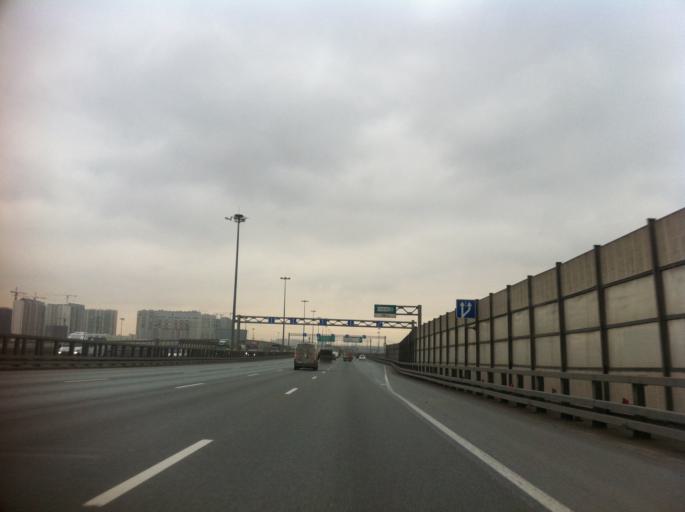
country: RU
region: St.-Petersburg
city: Shushary
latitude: 59.8170
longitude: 30.3867
